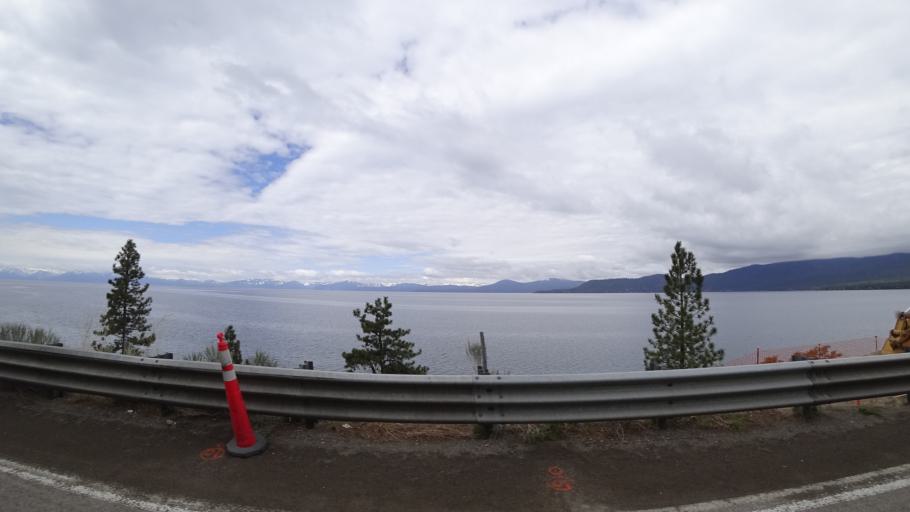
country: US
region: Nevada
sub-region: Washoe County
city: Incline Village
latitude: 39.2152
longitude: -119.9288
